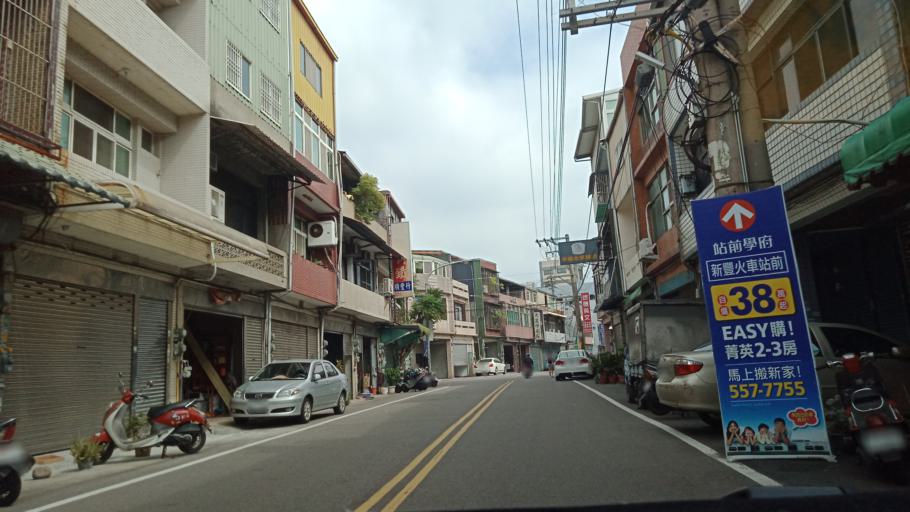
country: TW
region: Taiwan
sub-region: Hsinchu
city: Zhubei
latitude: 24.8731
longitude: 120.9951
